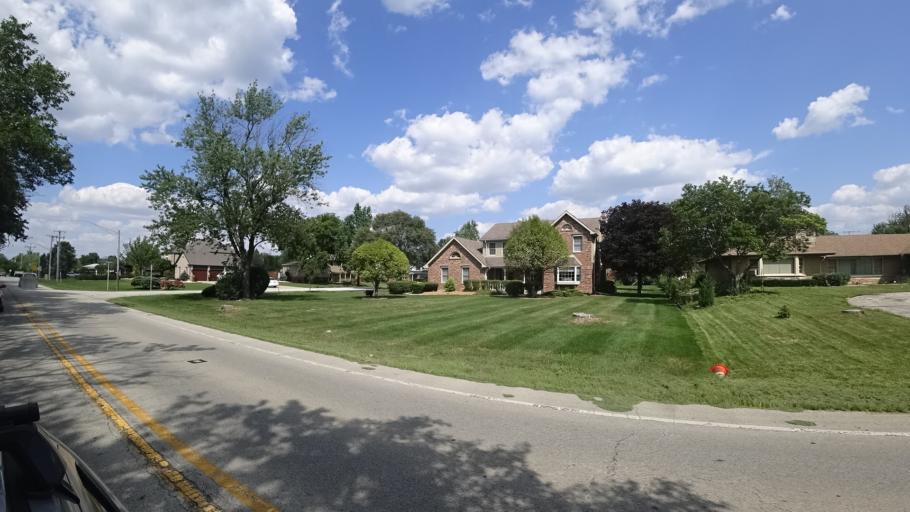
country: US
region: Illinois
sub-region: Cook County
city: Orland Park
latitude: 41.6193
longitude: -87.8192
